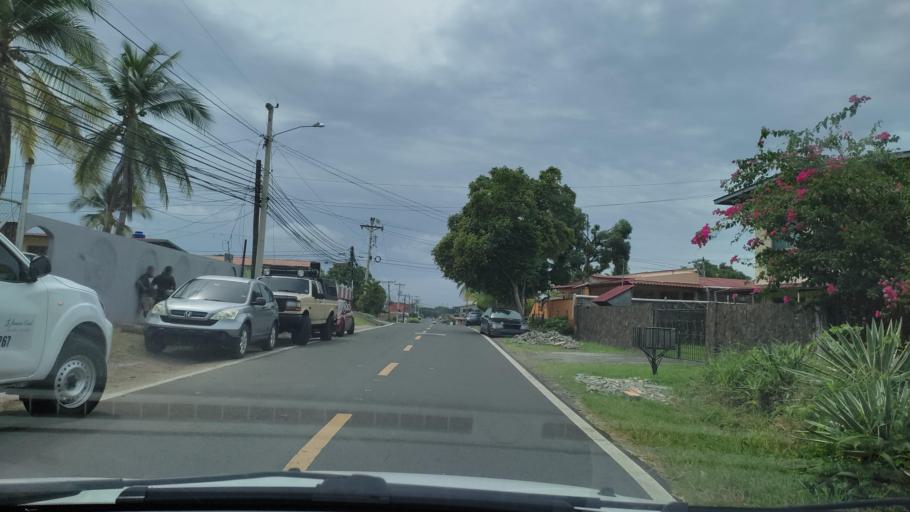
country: PA
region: Panama
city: San Miguelito
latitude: 9.0431
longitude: -79.4306
